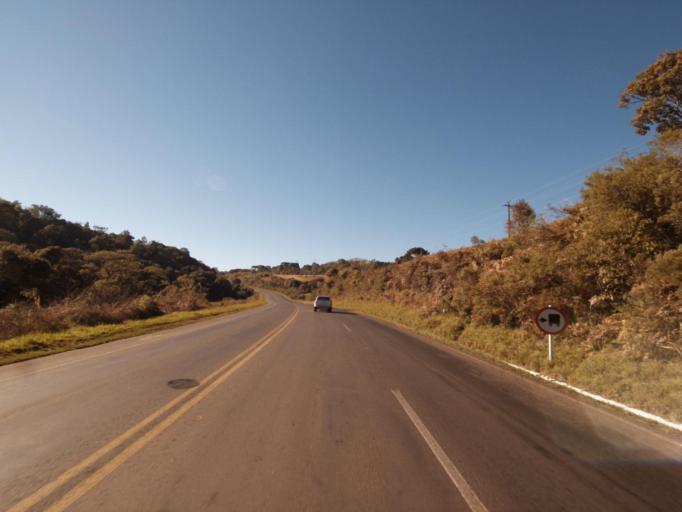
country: BR
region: Santa Catarina
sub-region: Concordia
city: Concordia
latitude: -26.8875
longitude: -51.9989
